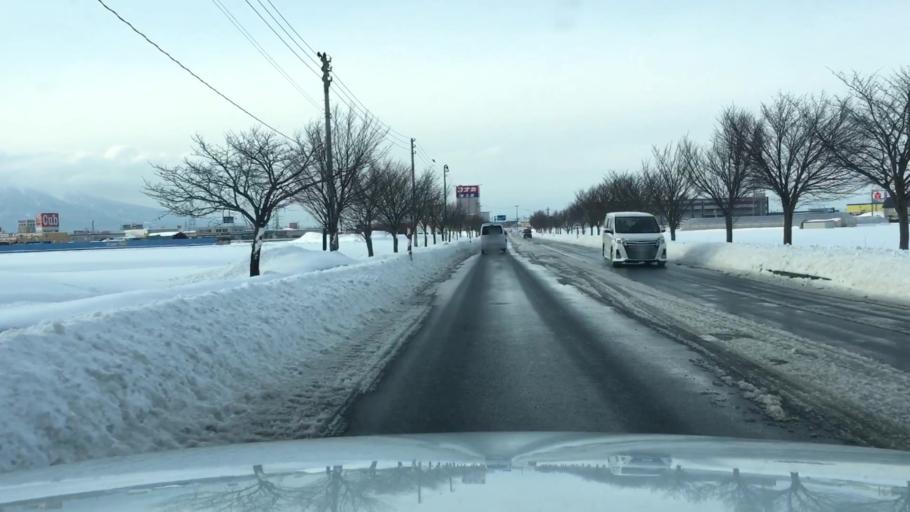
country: JP
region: Aomori
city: Hirosaki
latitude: 40.5958
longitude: 140.5172
